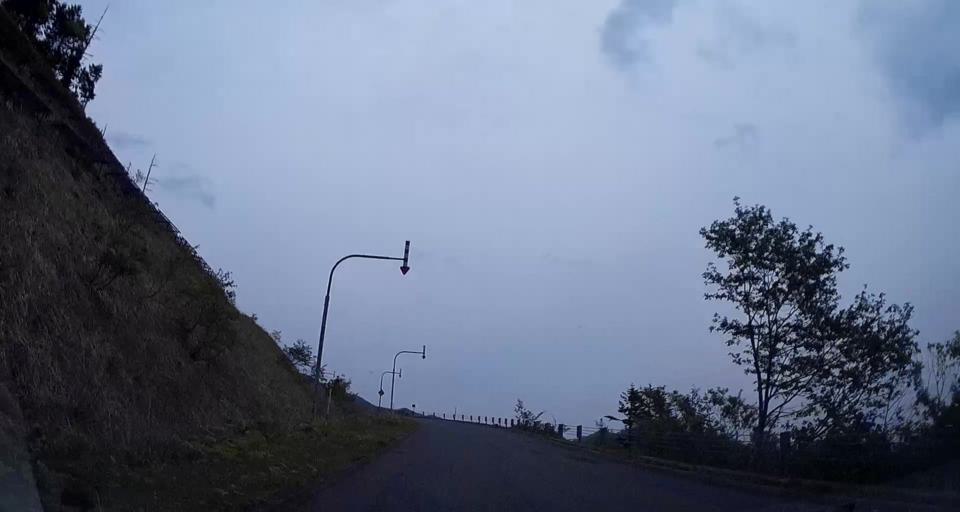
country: JP
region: Hokkaido
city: Shiraoi
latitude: 42.6620
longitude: 141.1645
